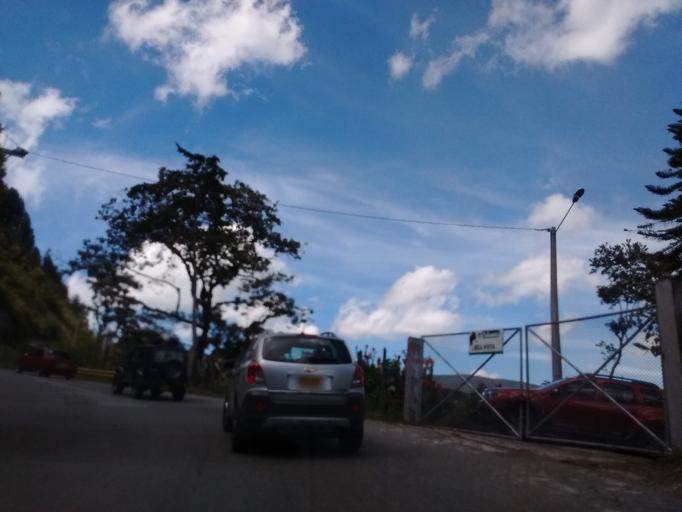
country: CO
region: Antioquia
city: Medellin
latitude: 6.2392
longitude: -75.5112
